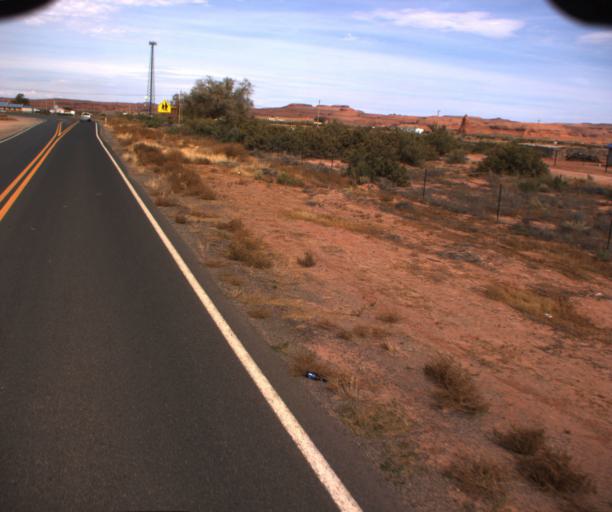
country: US
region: Arizona
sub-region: Apache County
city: Many Farms
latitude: 36.7167
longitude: -109.6259
